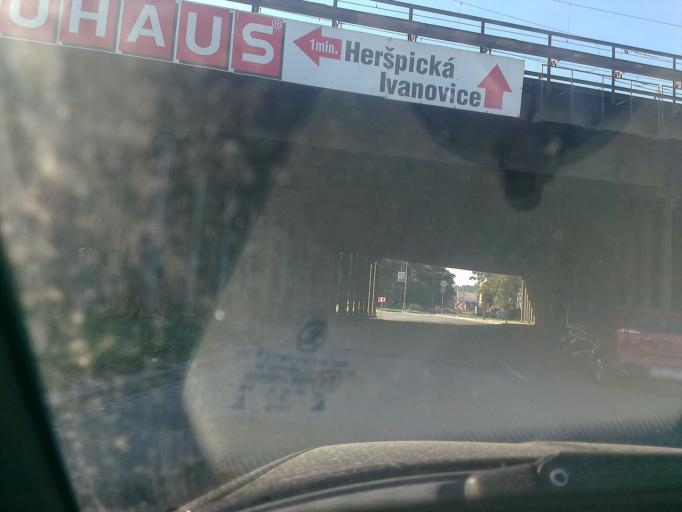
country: CZ
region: South Moravian
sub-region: Mesto Brno
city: Brno
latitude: 49.1836
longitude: 16.6077
